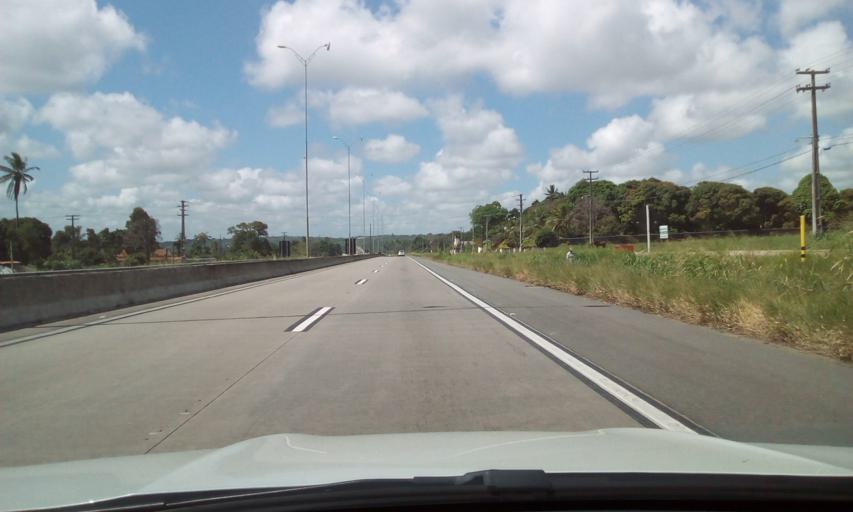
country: BR
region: Paraiba
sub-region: Alhandra
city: Alhandra
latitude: -7.3487
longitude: -34.9483
